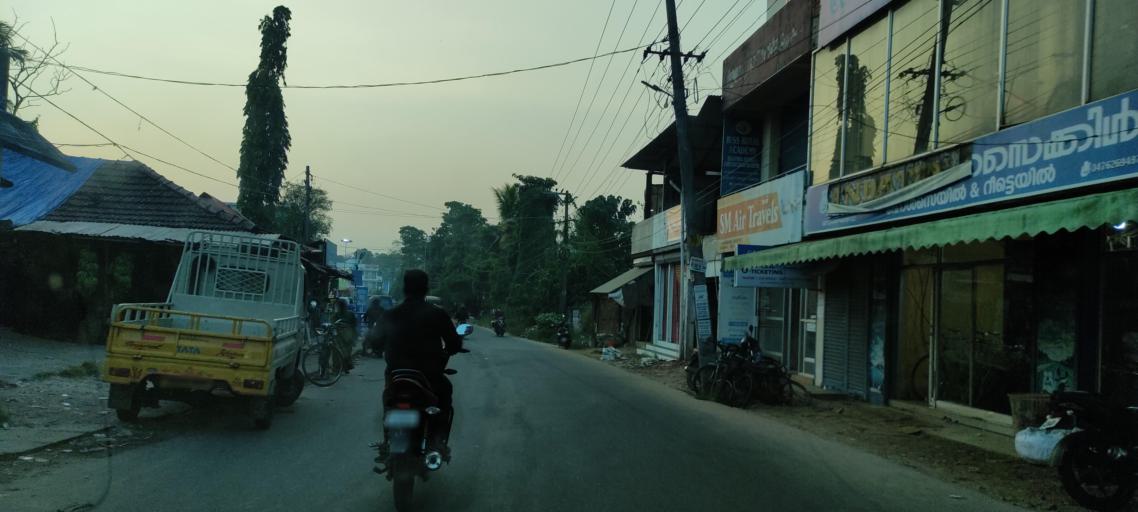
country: IN
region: Kerala
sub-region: Alappuzha
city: Kayankulam
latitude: 9.1349
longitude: 76.5117
